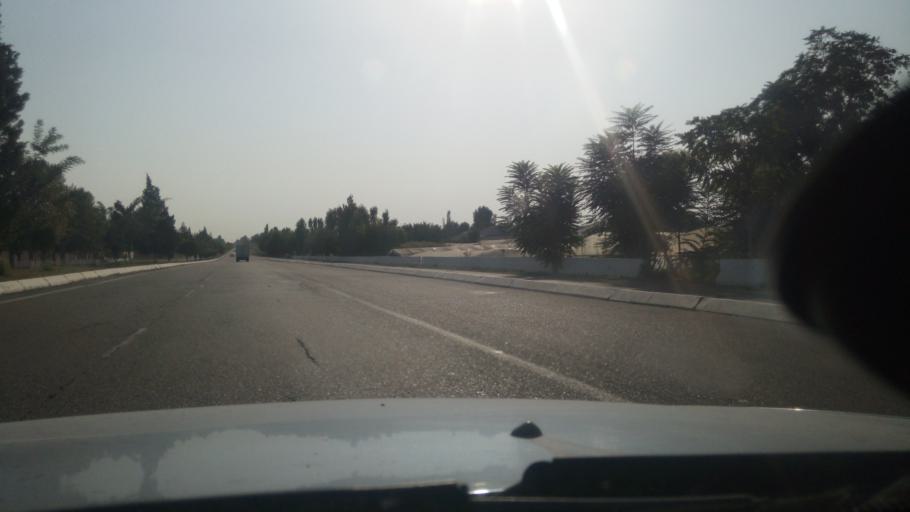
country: UZ
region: Toshkent
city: Zafar
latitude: 41.0100
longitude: 68.8370
